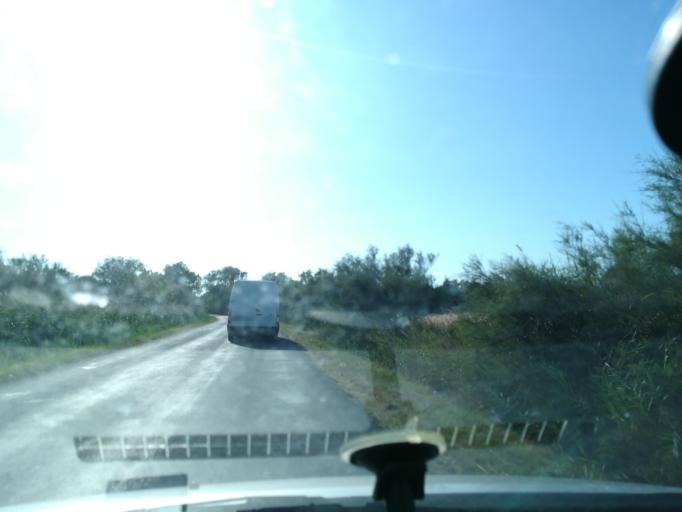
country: FR
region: Languedoc-Roussillon
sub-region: Departement de l'Herault
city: Vias
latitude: 43.2948
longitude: 3.3975
